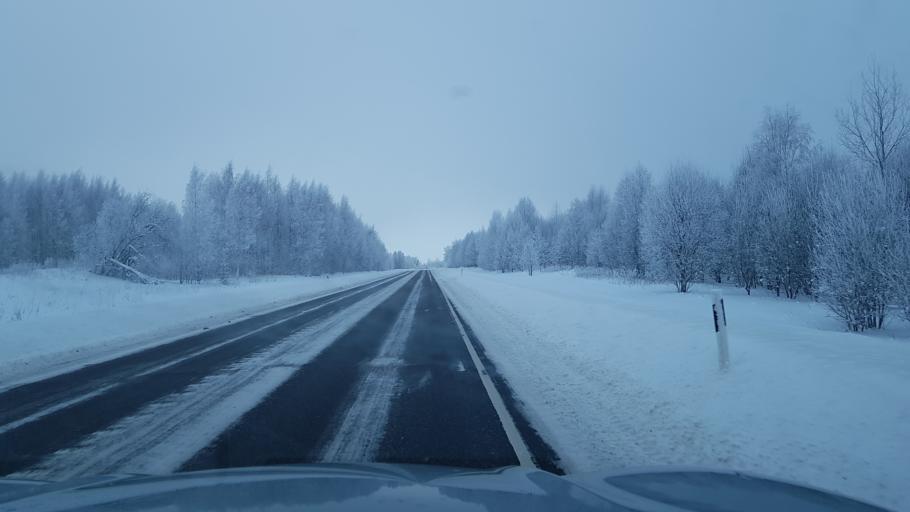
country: EE
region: Ida-Virumaa
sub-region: Johvi vald
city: Johvi
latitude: 59.2128
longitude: 27.3408
